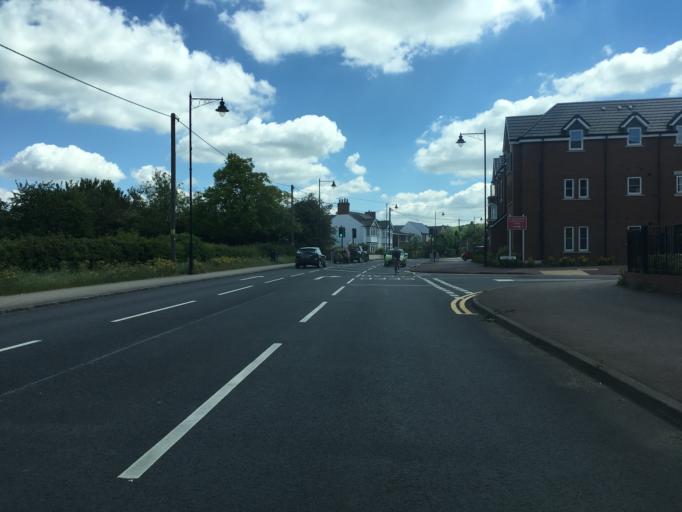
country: GB
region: England
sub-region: Milton Keynes
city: Woburn Sands
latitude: 52.0173
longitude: -0.6515
